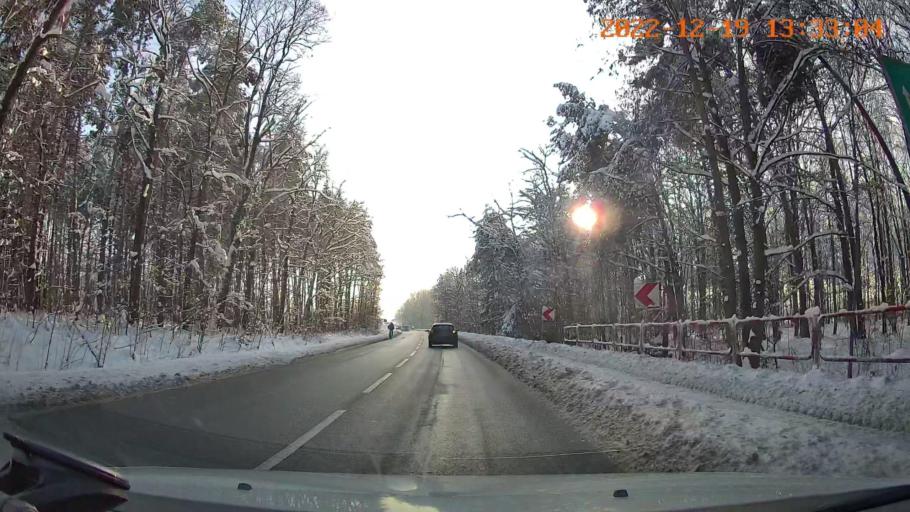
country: PL
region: Silesian Voivodeship
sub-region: Powiat bierunsko-ledzinski
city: Bierun
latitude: 50.1066
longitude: 19.0984
